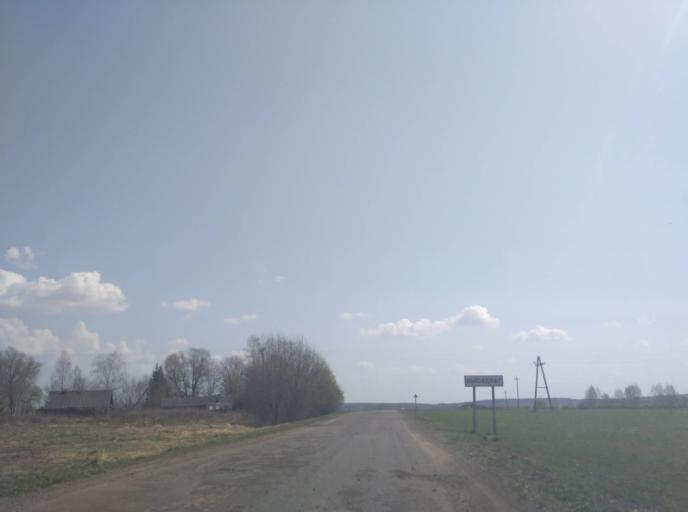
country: BY
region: Minsk
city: Loshnitsa
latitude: 54.4916
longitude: 28.7234
